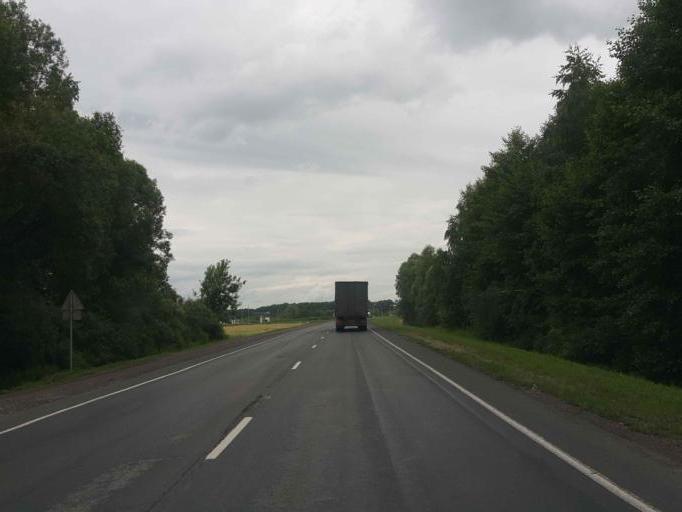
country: RU
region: Tambov
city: Zavoronezhskoye
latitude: 52.9329
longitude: 40.6097
